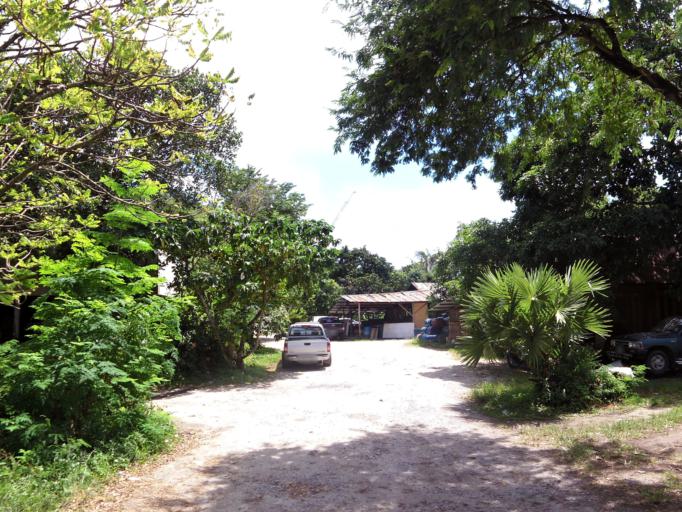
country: TH
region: Phuket
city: Ban Chalong
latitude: 7.8259
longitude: 98.3391
